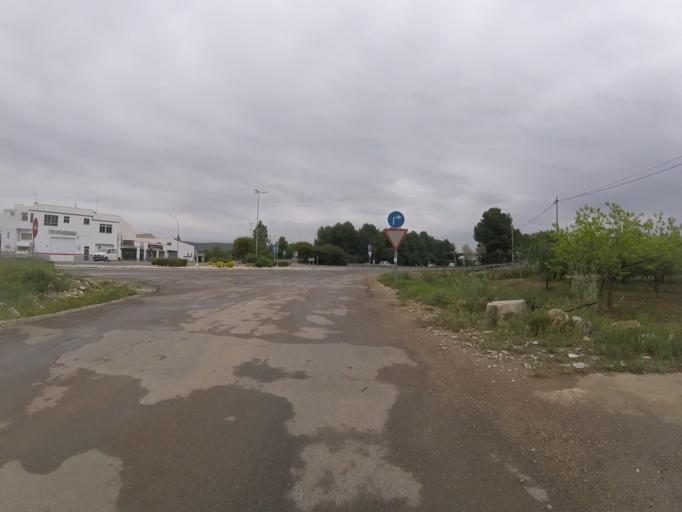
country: ES
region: Valencia
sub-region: Provincia de Castello
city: Alcala de Xivert
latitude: 40.2976
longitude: 0.2274
